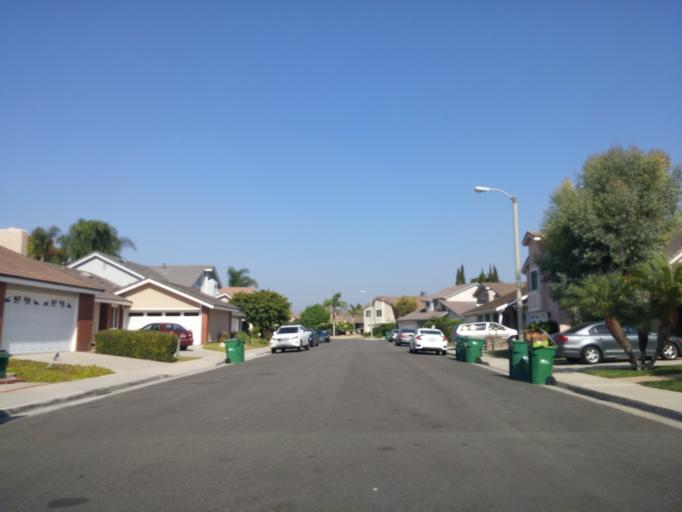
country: US
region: California
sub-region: Orange County
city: Irvine
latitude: 33.6872
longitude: -117.7880
